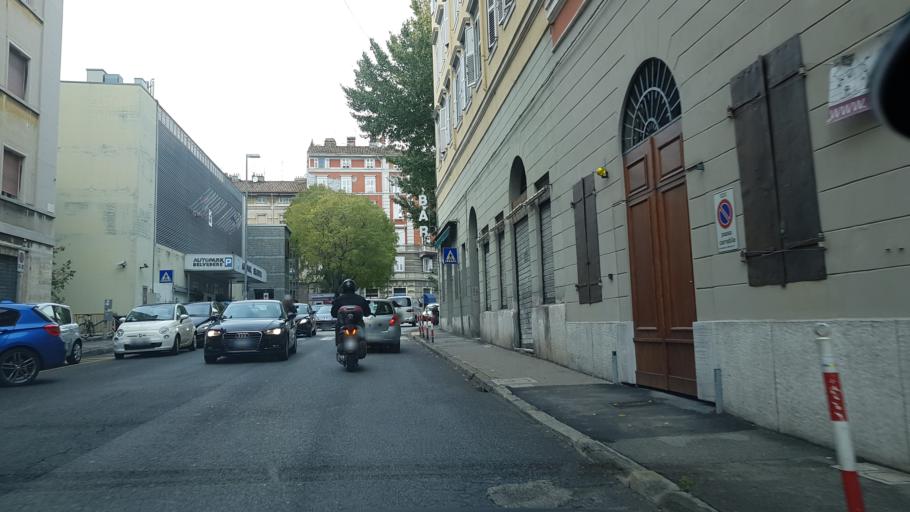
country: IT
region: Friuli Venezia Giulia
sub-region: Provincia di Trieste
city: Trieste
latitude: 45.6587
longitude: 13.7732
